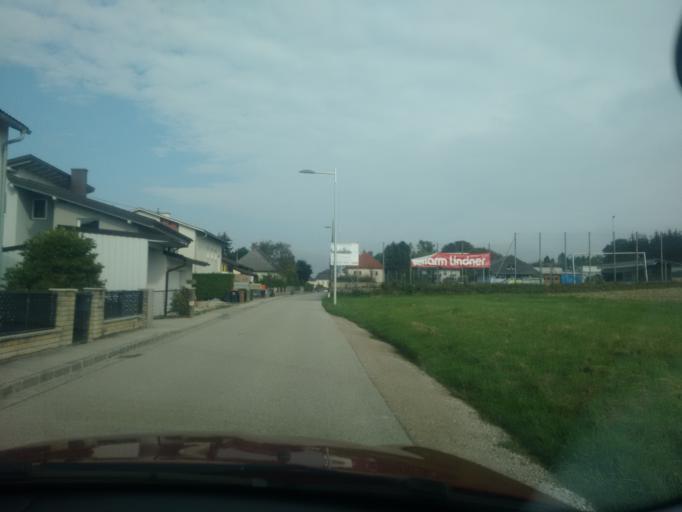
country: AT
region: Upper Austria
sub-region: Wels-Land
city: Steinhaus
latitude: 48.1130
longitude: 14.0222
